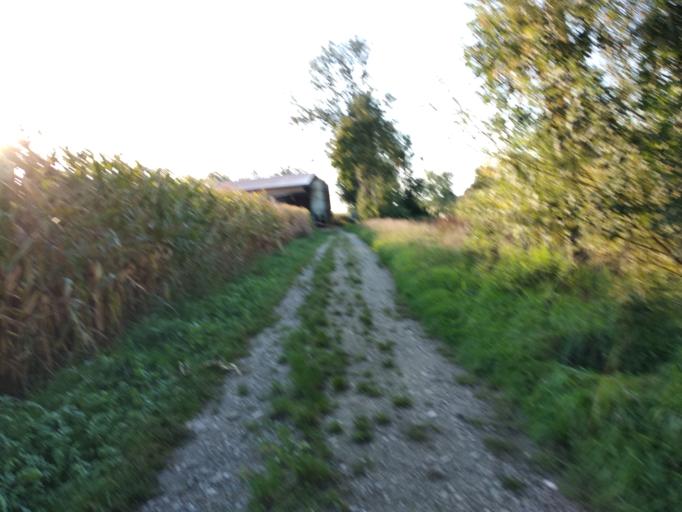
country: DE
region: Bavaria
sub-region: Upper Bavaria
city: Steinhoring
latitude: 48.0896
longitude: 12.0419
